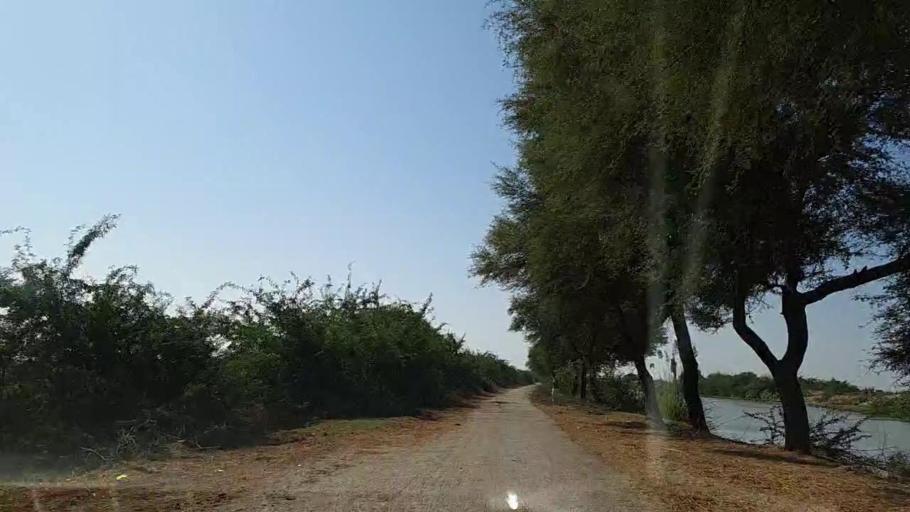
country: PK
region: Sindh
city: Chuhar Jamali
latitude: 24.5793
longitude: 68.0467
